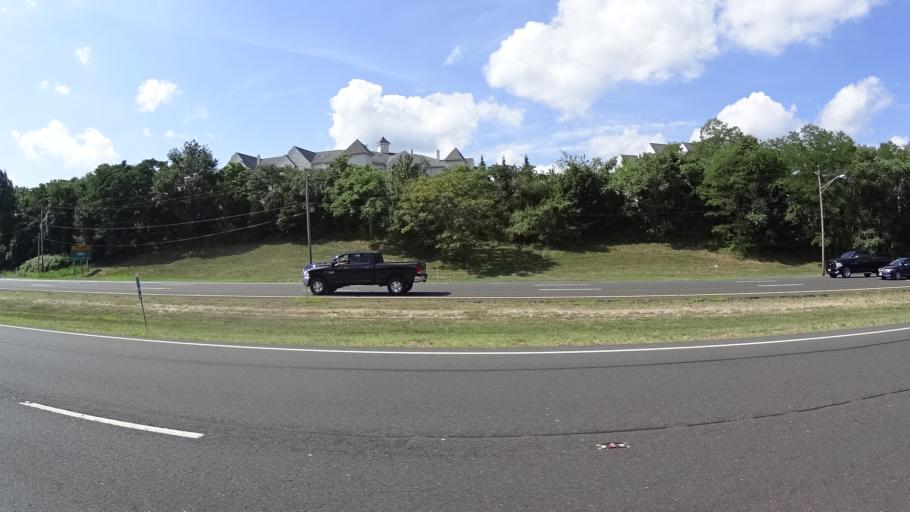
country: US
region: New Jersey
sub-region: Monmouth County
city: Matawan
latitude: 40.4227
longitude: -74.2162
